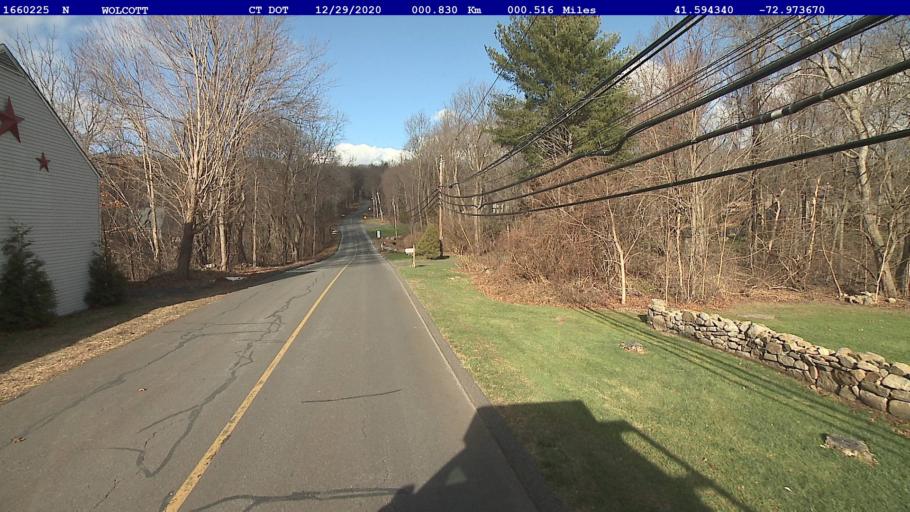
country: US
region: Connecticut
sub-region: New Haven County
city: Wolcott
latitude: 41.5943
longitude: -72.9737
